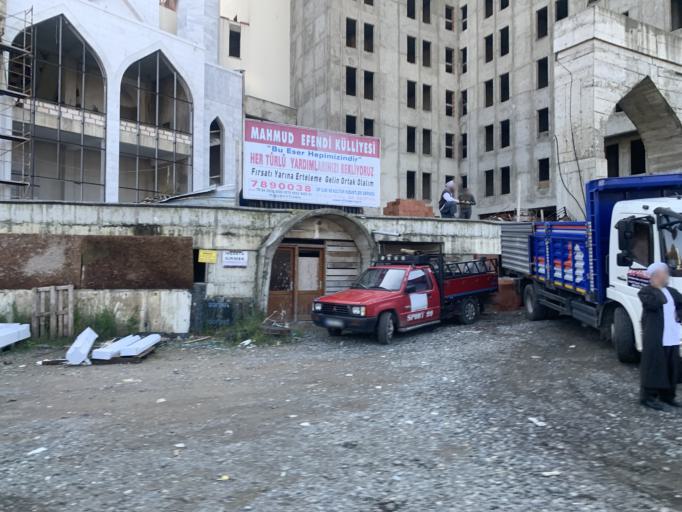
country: TR
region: Trabzon
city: Of
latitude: 40.9390
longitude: 40.2716
